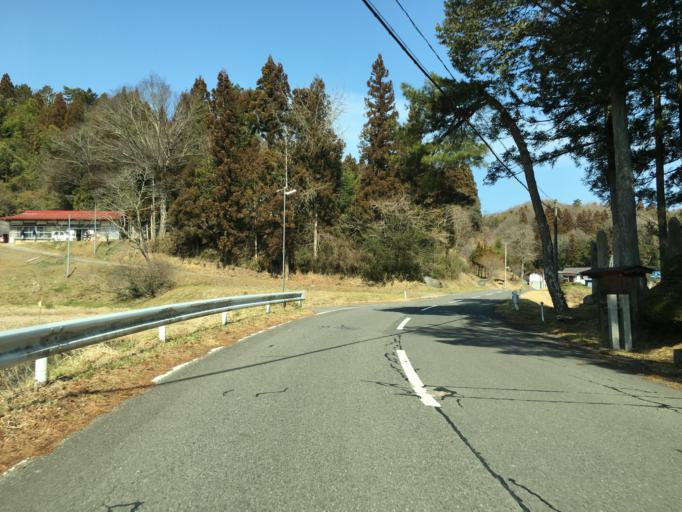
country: JP
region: Fukushima
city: Ishikawa
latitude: 37.0985
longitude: 140.4528
